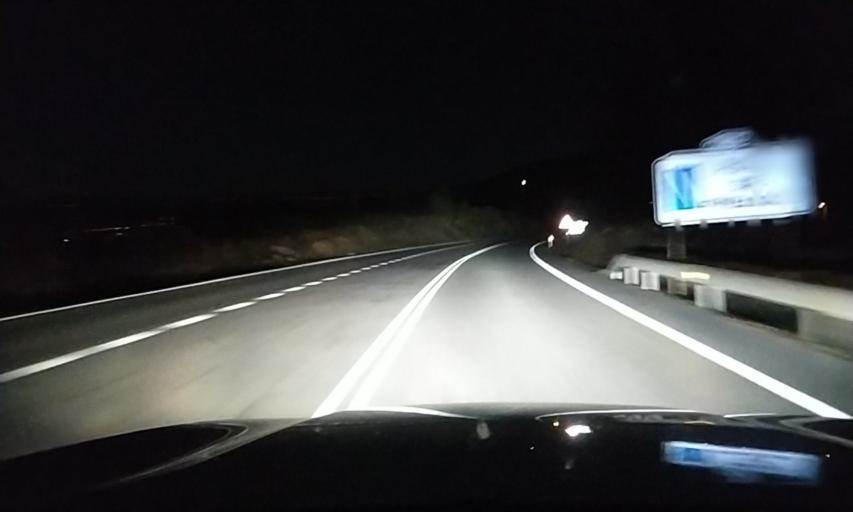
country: ES
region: Galicia
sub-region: Provincia de Ourense
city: Cualedro
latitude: 41.9748
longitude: -7.5201
